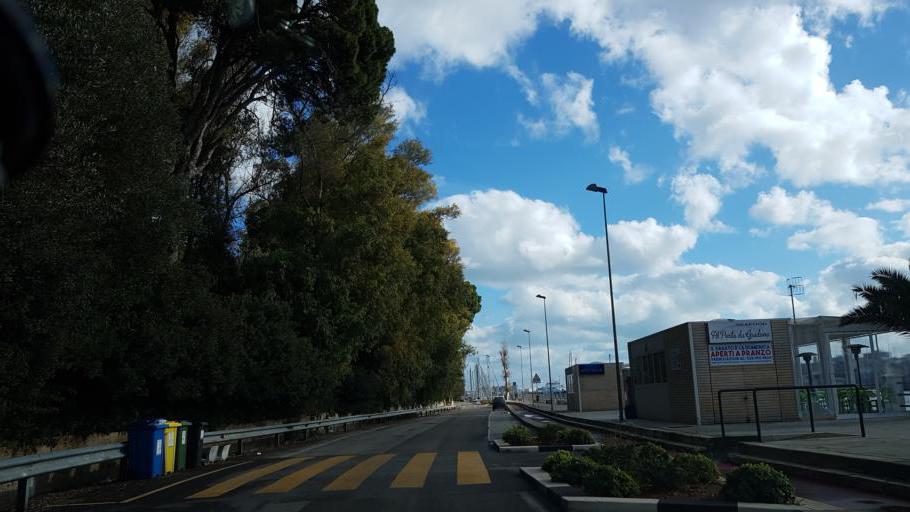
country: IT
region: Apulia
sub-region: Provincia di Brindisi
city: Brindisi
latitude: 40.6429
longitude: 17.9330
